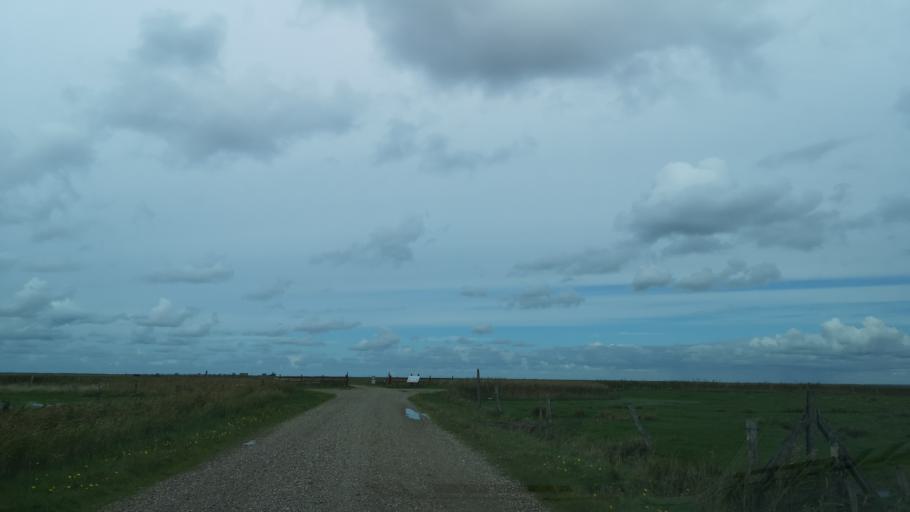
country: DK
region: Central Jutland
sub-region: Ringkobing-Skjern Kommune
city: Hvide Sande
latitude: 55.8732
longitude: 8.2275
